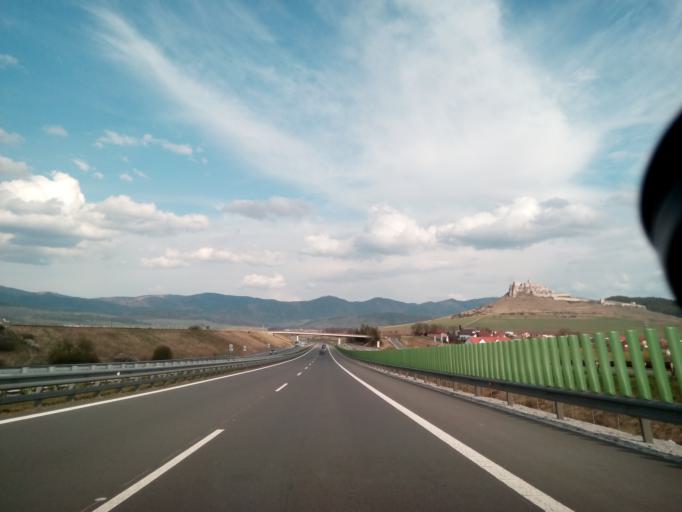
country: SK
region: Presovsky
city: Spisske Podhradie
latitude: 49.0082
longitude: 20.7407
